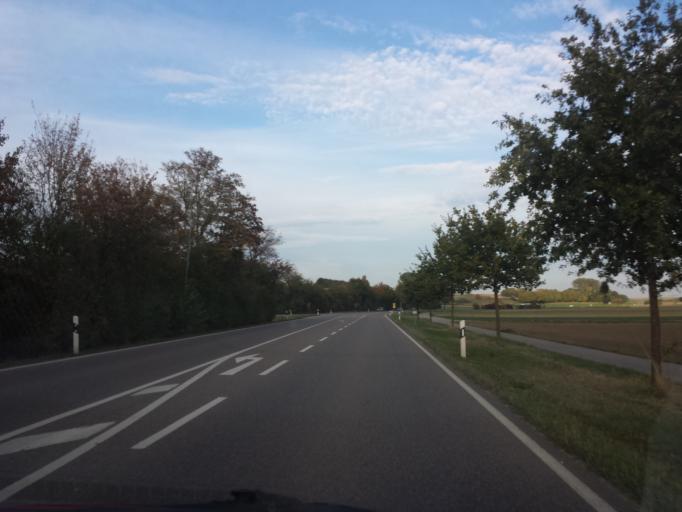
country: DE
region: Bavaria
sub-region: Upper Bavaria
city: Bergheim
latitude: 48.7661
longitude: 11.2803
